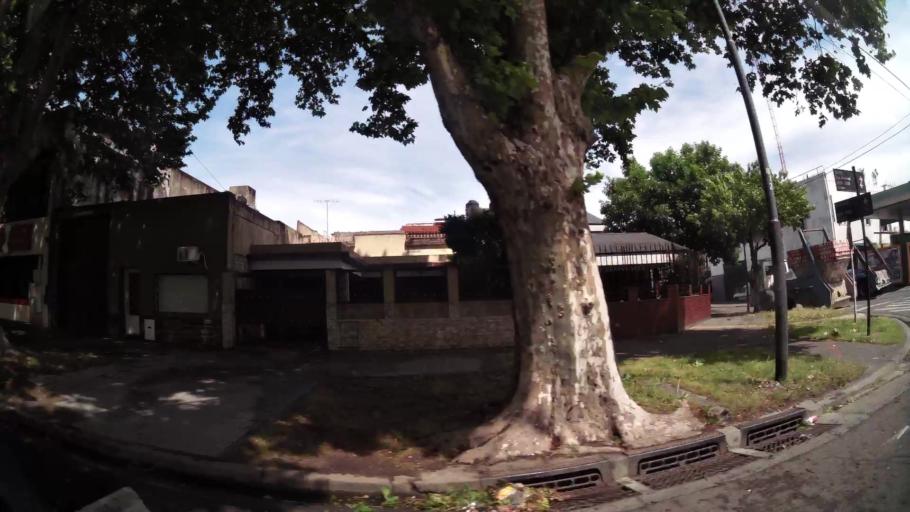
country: AR
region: Buenos Aires F.D.
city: Villa Lugano
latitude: -34.6614
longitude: -58.4306
